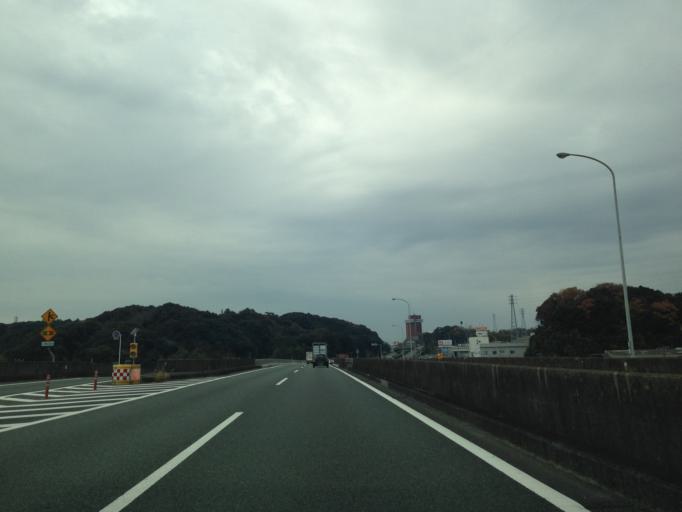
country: JP
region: Shizuoka
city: Fukuroi
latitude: 34.7394
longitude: 137.8886
